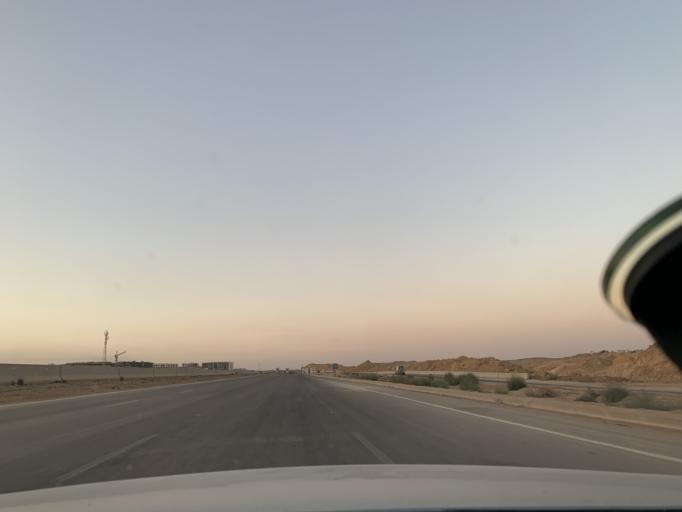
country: EG
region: Muhafazat al Qahirah
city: Halwan
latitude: 29.9601
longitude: 31.5453
